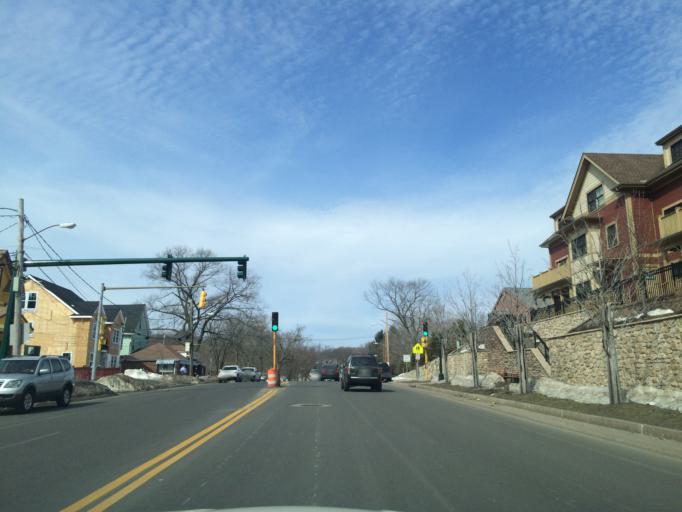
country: US
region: Massachusetts
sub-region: Middlesex County
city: Belmont
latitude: 42.3894
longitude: -71.1940
